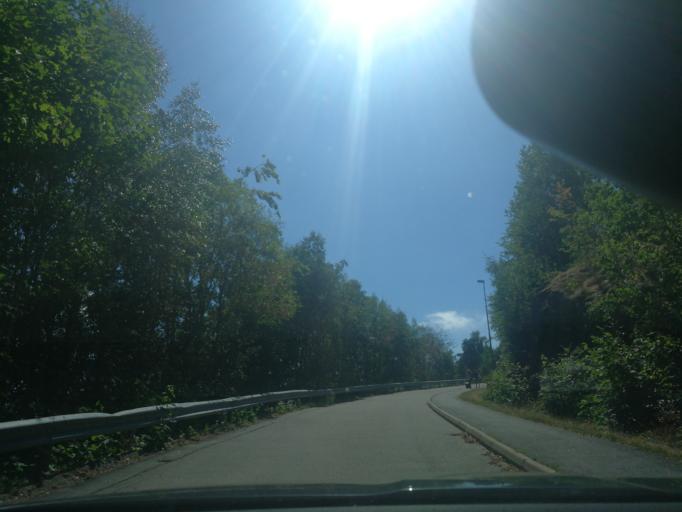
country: NO
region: Vestfold
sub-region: Stokke
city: Melsomvik
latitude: 59.2312
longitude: 10.3360
